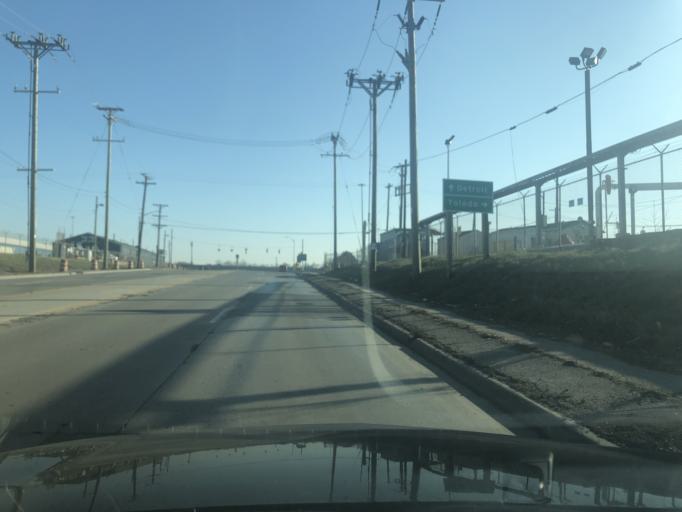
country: US
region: Michigan
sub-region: Wayne County
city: Melvindale
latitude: 42.2792
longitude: -83.1588
